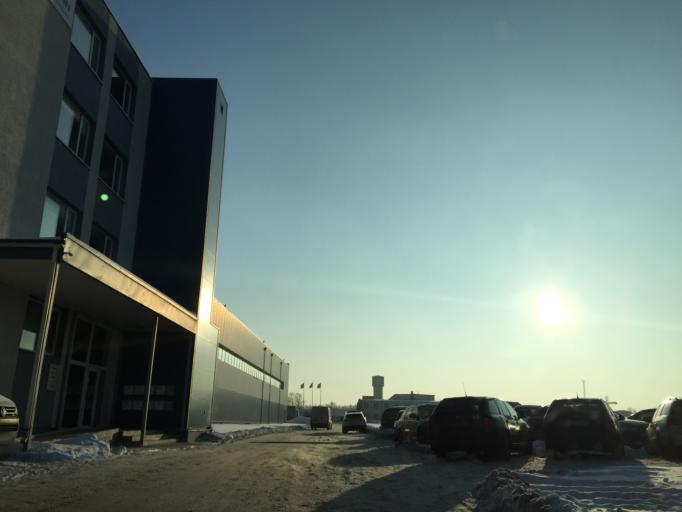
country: LV
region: Stopini
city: Ulbroka
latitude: 56.9257
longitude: 24.2003
